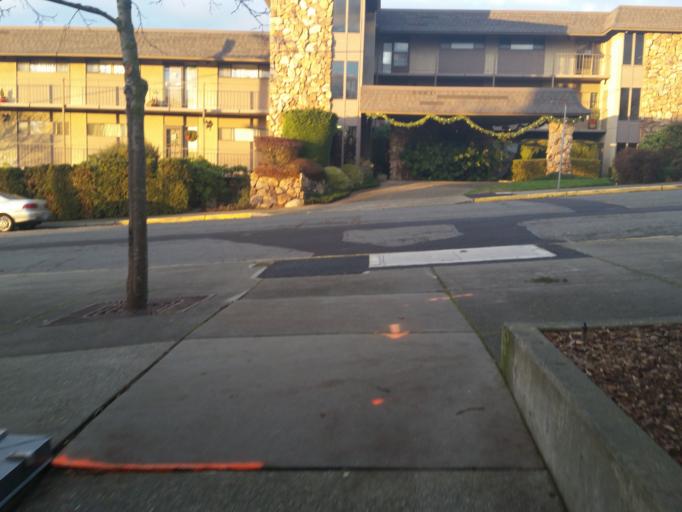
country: US
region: Washington
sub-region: Snohomish County
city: Edmonds
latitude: 47.8104
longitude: -122.3726
